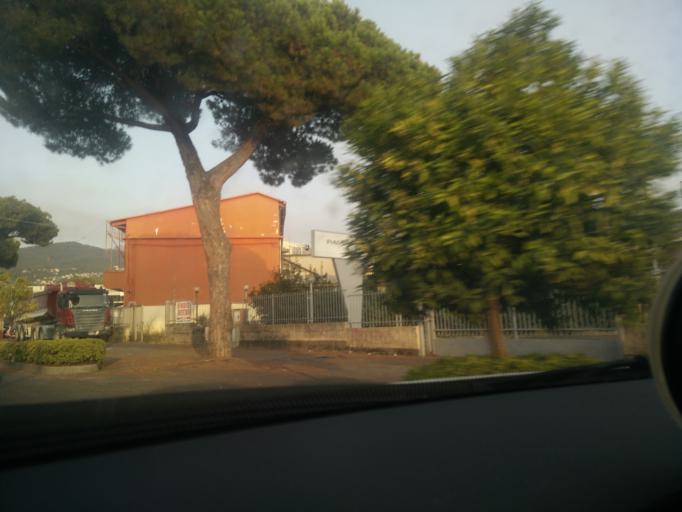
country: IT
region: Tuscany
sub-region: Provincia di Massa-Carrara
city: Massa
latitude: 44.0376
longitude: 10.1114
